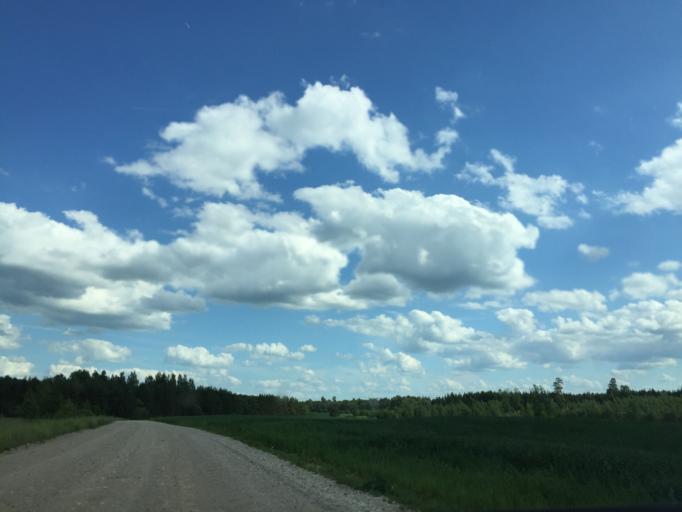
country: LV
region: Jaunpils
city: Jaunpils
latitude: 56.8131
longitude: 23.0742
